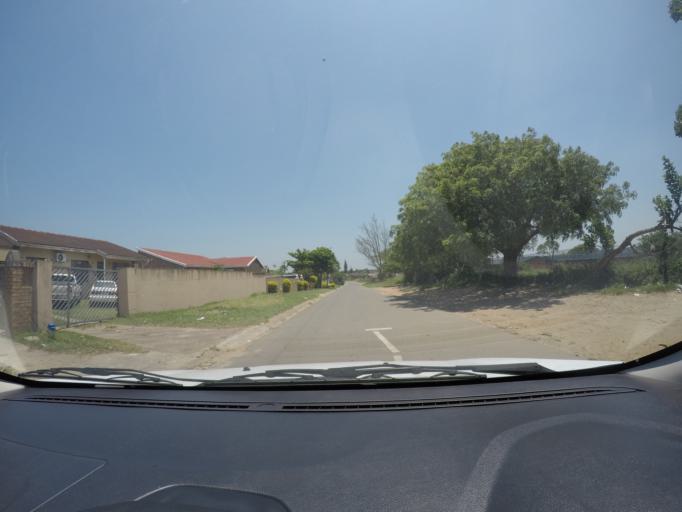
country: ZA
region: KwaZulu-Natal
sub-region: uThungulu District Municipality
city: eSikhawini
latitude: -28.8843
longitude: 31.8970
